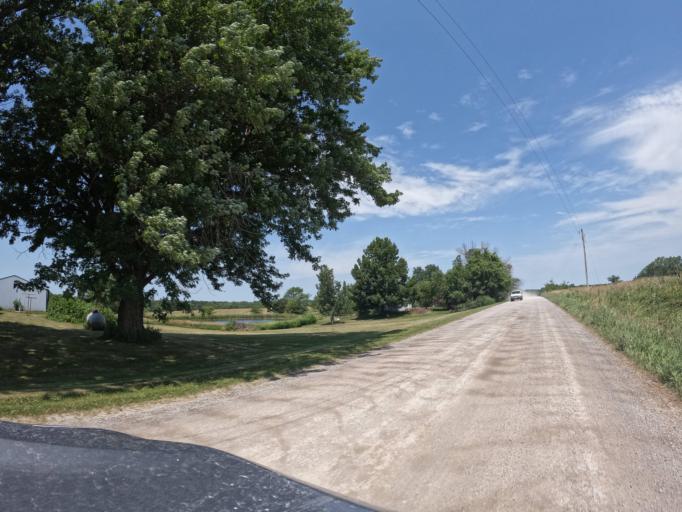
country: US
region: Iowa
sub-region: Appanoose County
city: Centerville
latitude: 40.7933
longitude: -92.9160
